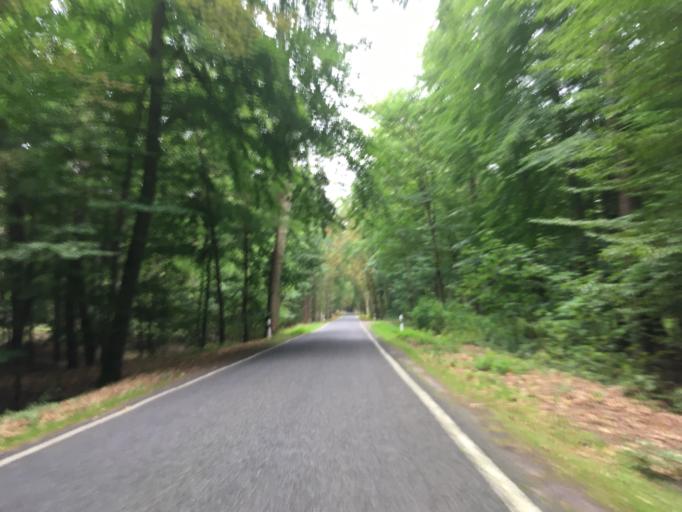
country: DE
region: Brandenburg
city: Angermunde
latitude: 53.0521
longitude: 13.8933
